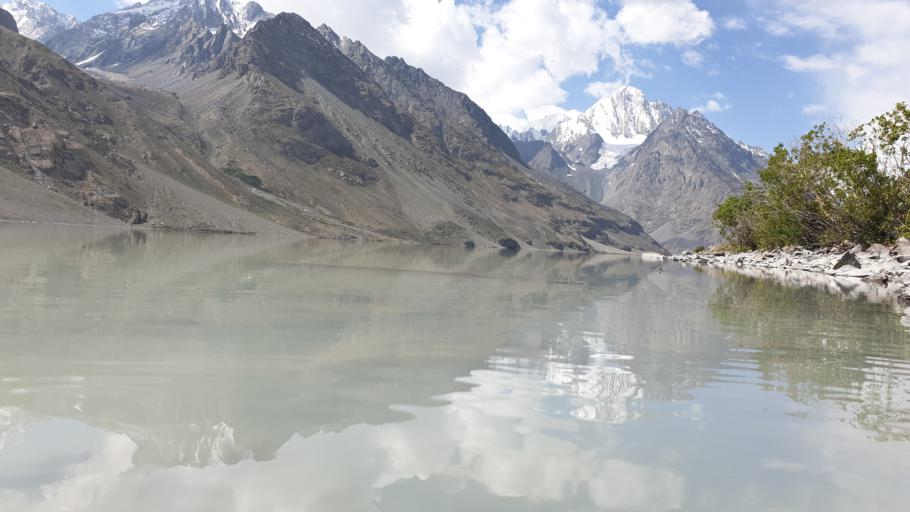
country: PK
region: Khyber Pakhtunkhwa
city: Tal
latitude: 35.9186
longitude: 72.3397
